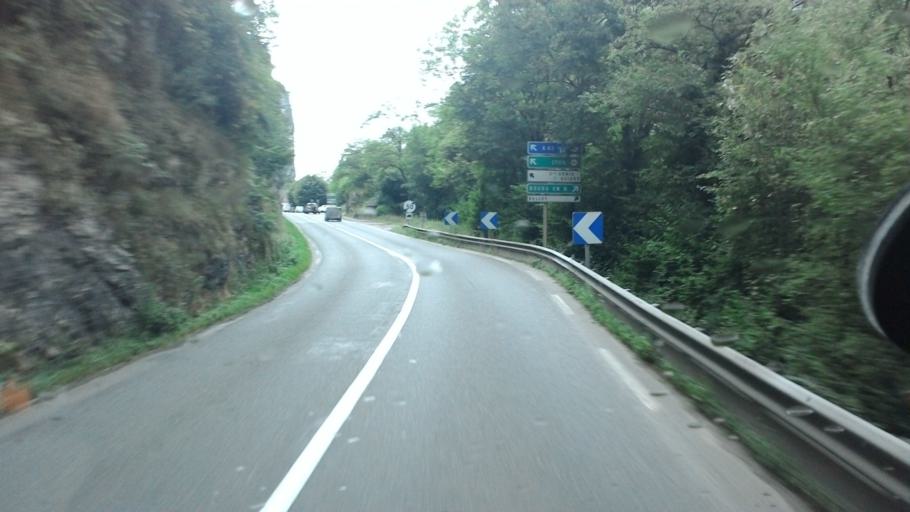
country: FR
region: Rhone-Alpes
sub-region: Departement de la Savoie
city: Yenne
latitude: 45.7094
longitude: 5.7305
